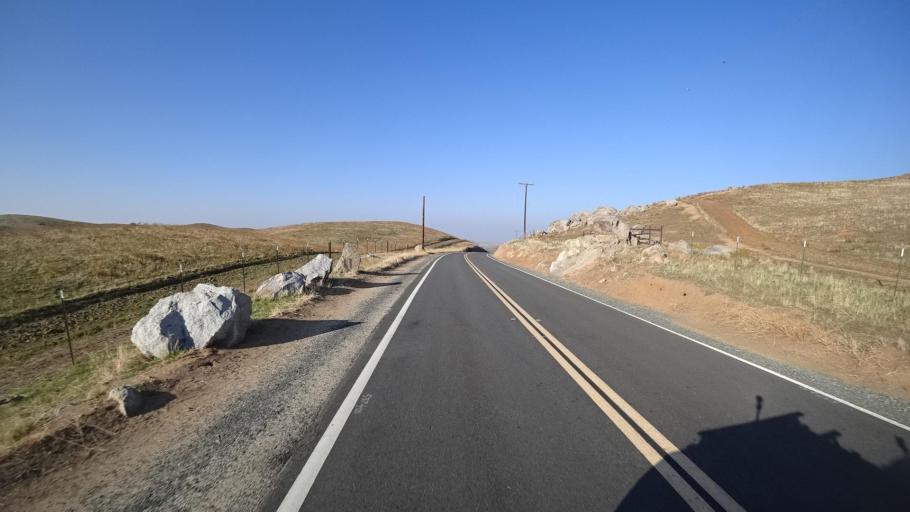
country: US
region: California
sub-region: Tulare County
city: Richgrove
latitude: 35.7420
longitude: -118.8924
